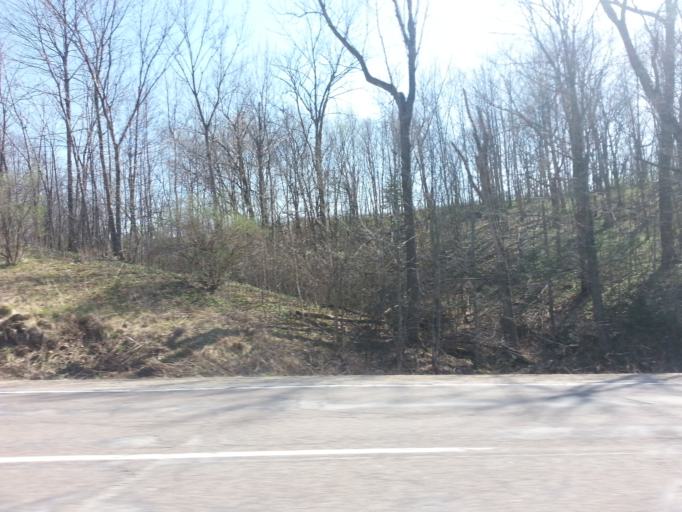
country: US
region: Wisconsin
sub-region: Pepin County
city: Durand
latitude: 44.6415
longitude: -92.1566
